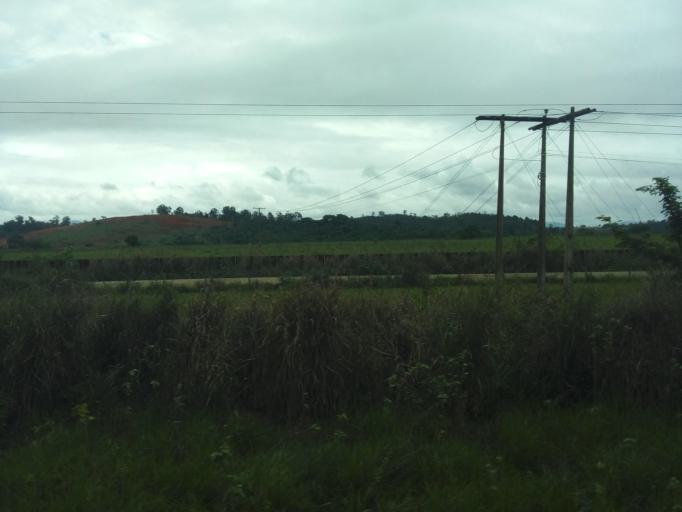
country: BR
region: Minas Gerais
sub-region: Ipatinga
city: Ipatinga
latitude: -19.4677
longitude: -42.4788
